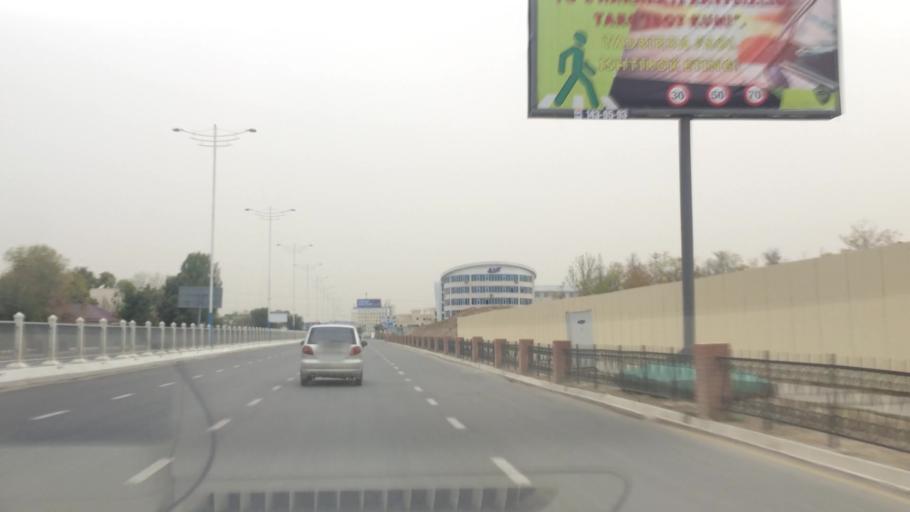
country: UZ
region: Toshkent
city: Salor
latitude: 41.3038
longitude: 69.3143
